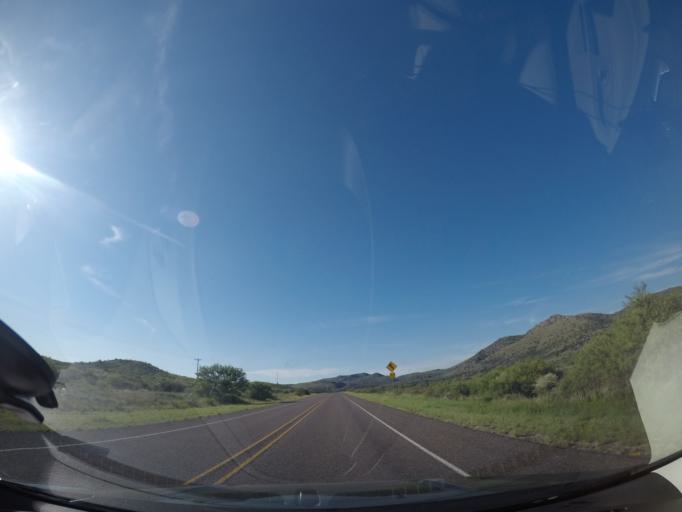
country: US
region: Texas
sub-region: Brewster County
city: Alpine
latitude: 30.3173
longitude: -103.6258
